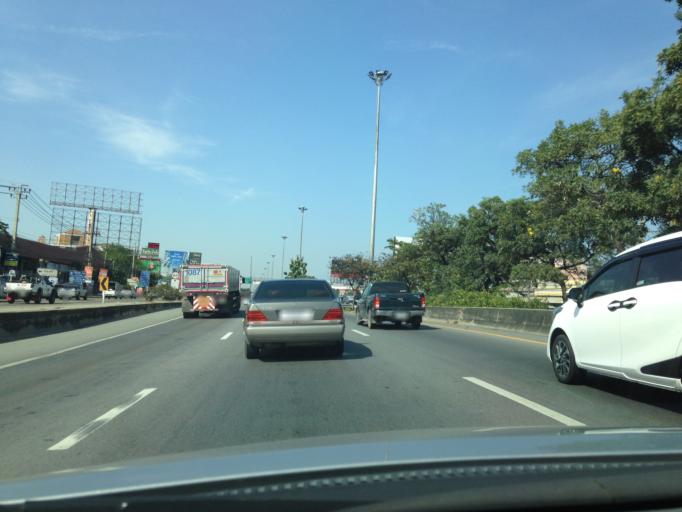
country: TH
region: Nonthaburi
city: Bang Yai
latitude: 13.8355
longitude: 100.4135
